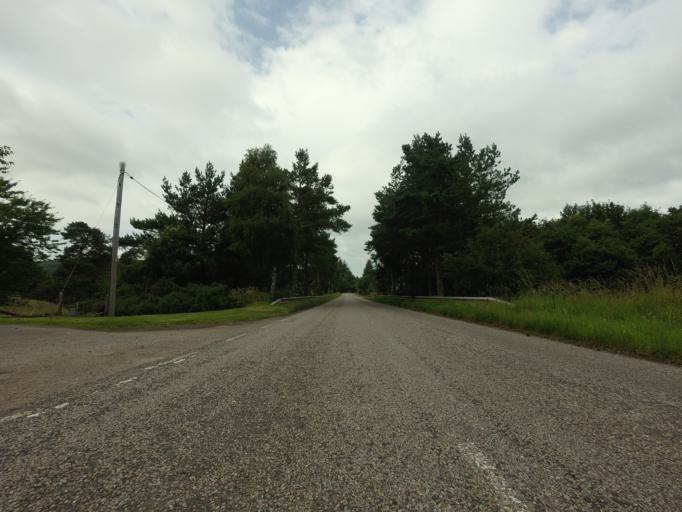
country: GB
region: Scotland
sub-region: Highland
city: Evanton
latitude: 57.9413
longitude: -4.4070
